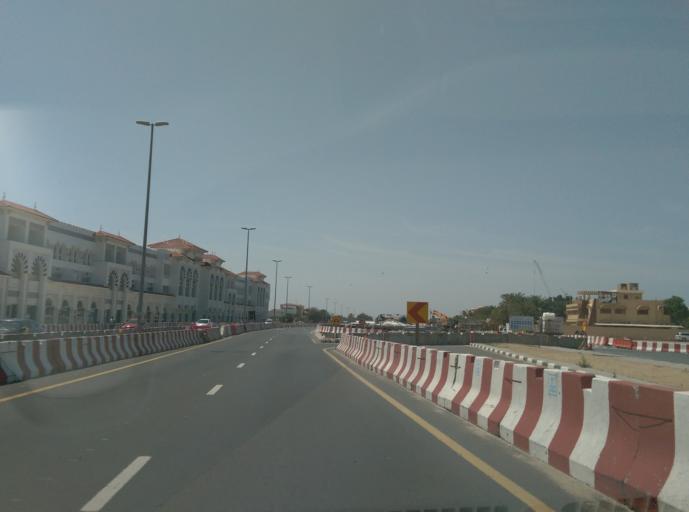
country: AE
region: Dubai
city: Dubai
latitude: 25.1951
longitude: 55.2453
